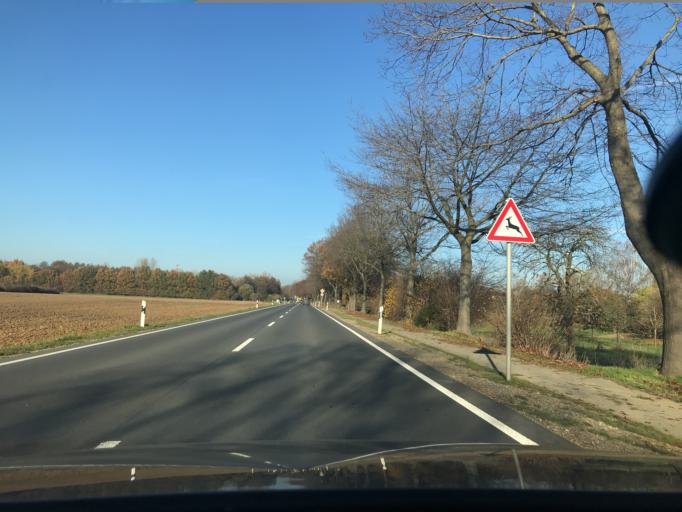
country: DE
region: North Rhine-Westphalia
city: Kempen
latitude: 51.4011
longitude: 6.4194
